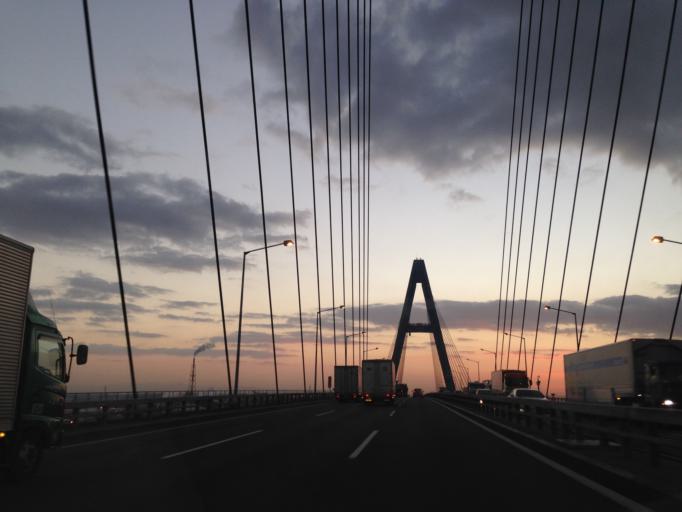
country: JP
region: Aichi
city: Obu
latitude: 35.0539
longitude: 136.8764
